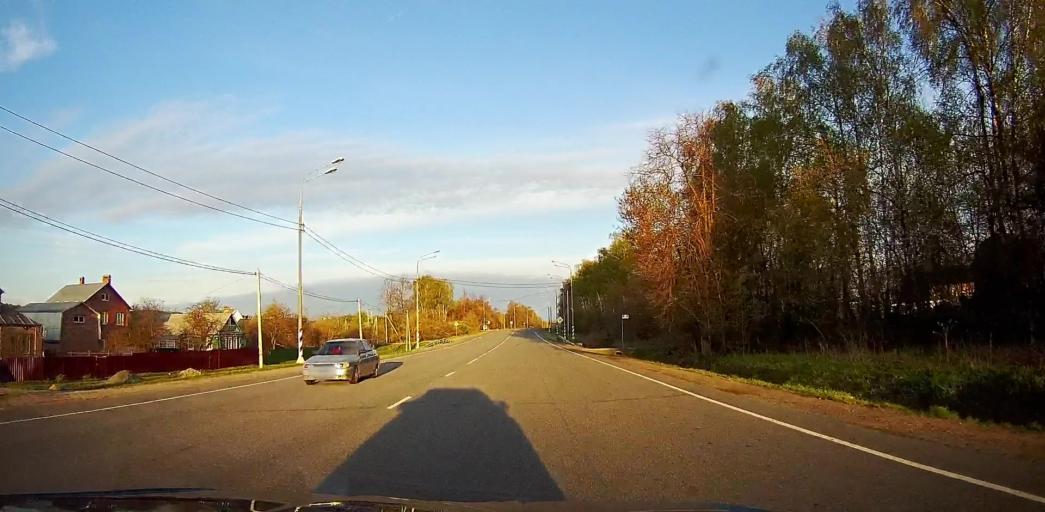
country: RU
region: Moskovskaya
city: Troitskoye
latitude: 55.2236
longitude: 38.5716
